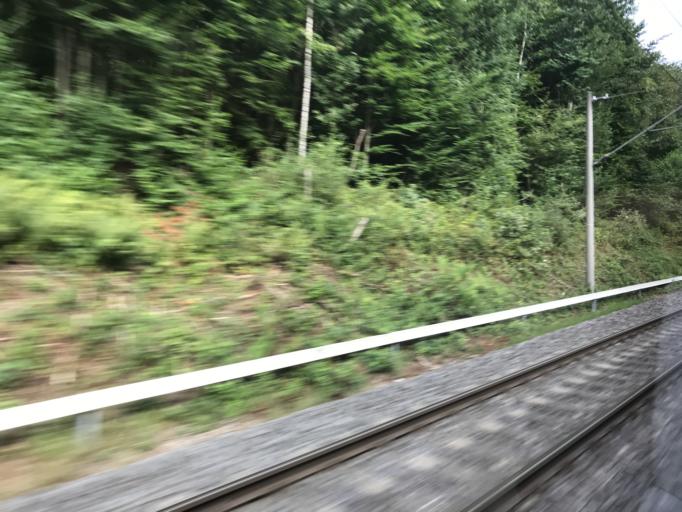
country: DE
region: Hesse
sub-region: Regierungsbezirk Darmstadt
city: Idstein
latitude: 50.2030
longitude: 8.2611
